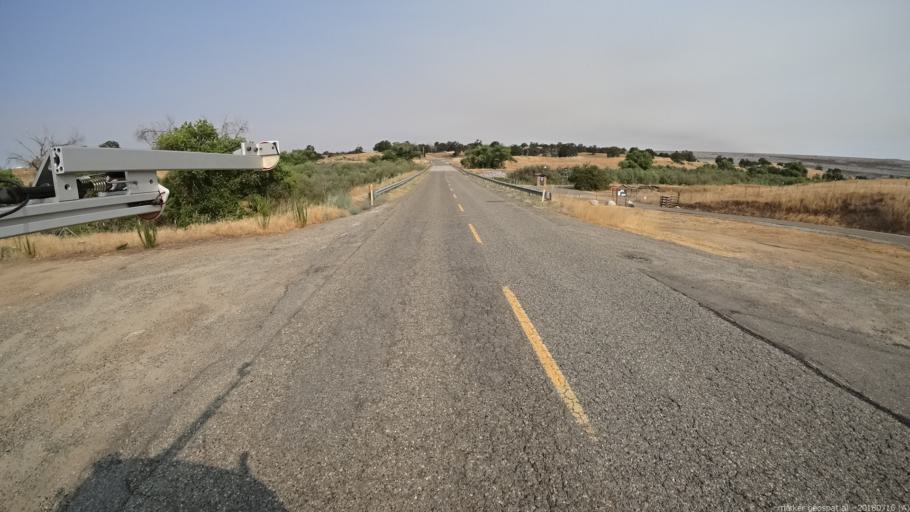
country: US
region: California
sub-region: Madera County
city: Bonadelle Ranchos-Madera Ranchos
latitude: 37.1033
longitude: -119.8872
